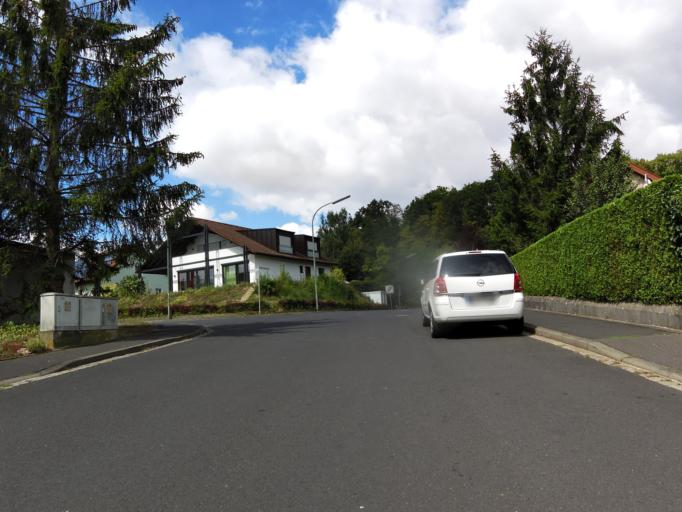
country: DE
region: Bavaria
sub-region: Regierungsbezirk Unterfranken
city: Hochberg
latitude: 49.7851
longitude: 9.8753
